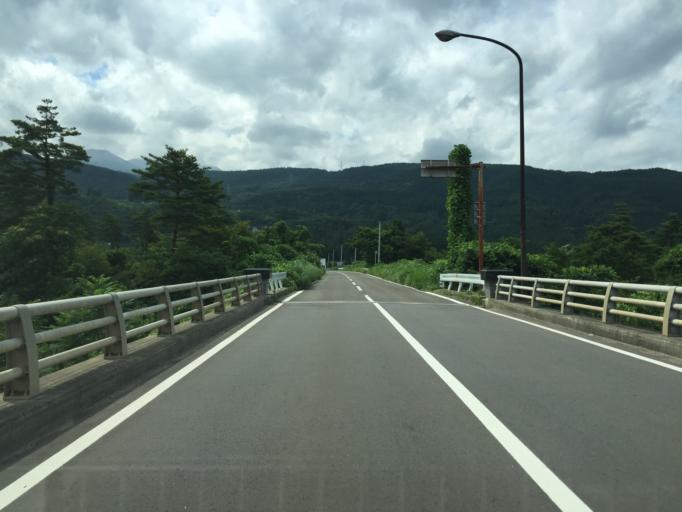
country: JP
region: Fukushima
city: Fukushima-shi
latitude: 37.7104
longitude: 140.3553
